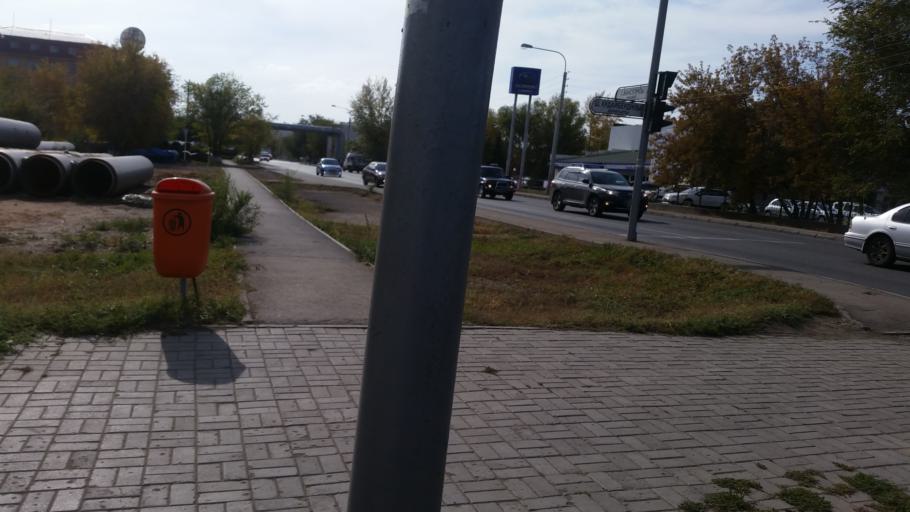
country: KZ
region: Astana Qalasy
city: Astana
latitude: 51.1624
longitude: 71.4834
